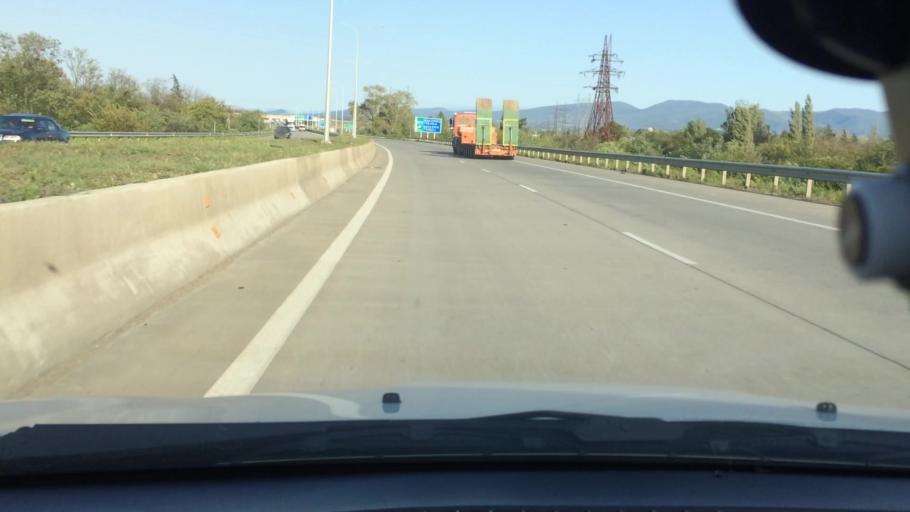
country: GE
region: Imereti
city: Zestap'oni
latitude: 42.1537
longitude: 42.9580
